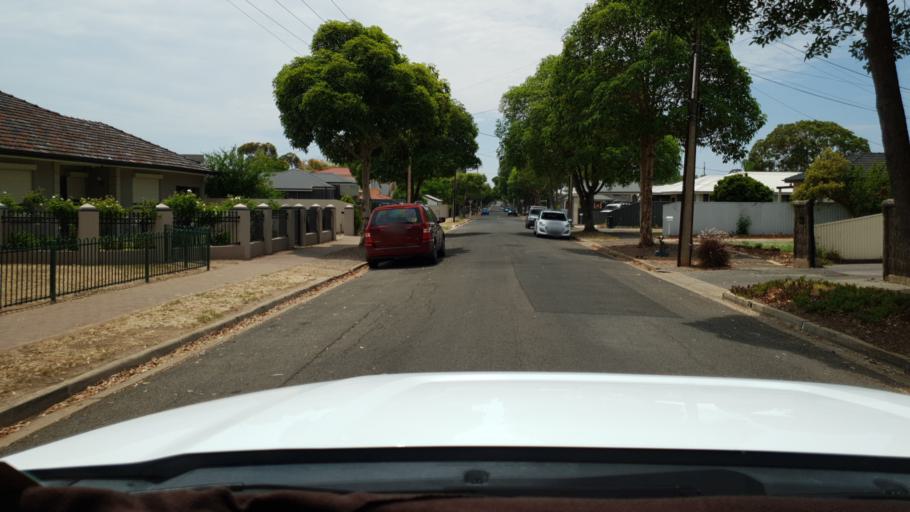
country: AU
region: South Australia
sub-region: Marion
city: Clovelly Park
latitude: -34.9974
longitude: 138.5802
